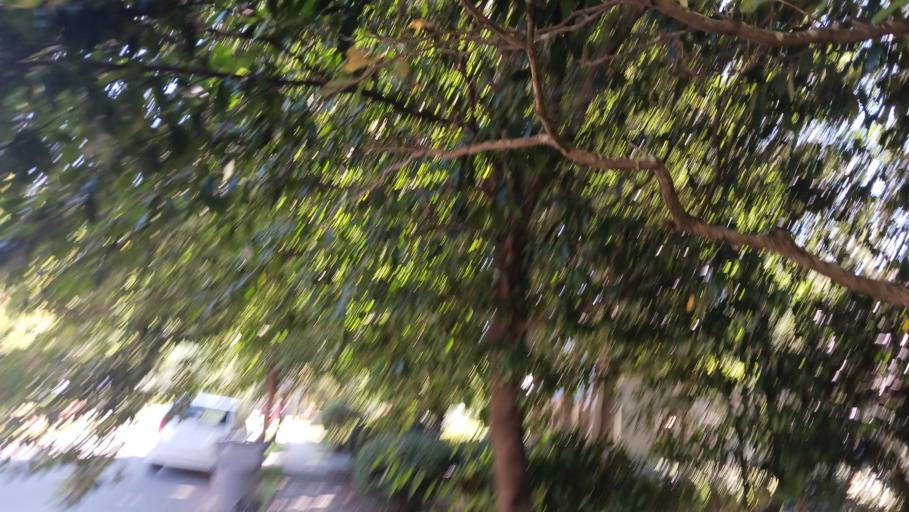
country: US
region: North Carolina
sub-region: Mecklenburg County
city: Charlotte
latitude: 35.2101
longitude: -80.8171
